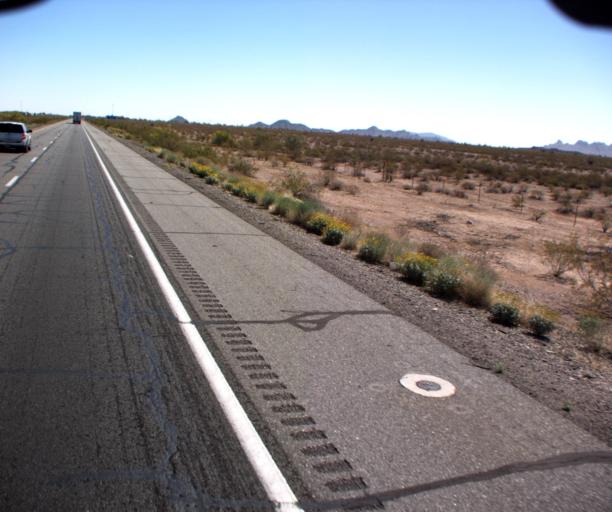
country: US
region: Arizona
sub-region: Maricopa County
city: Buckeye
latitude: 33.5227
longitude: -113.0842
